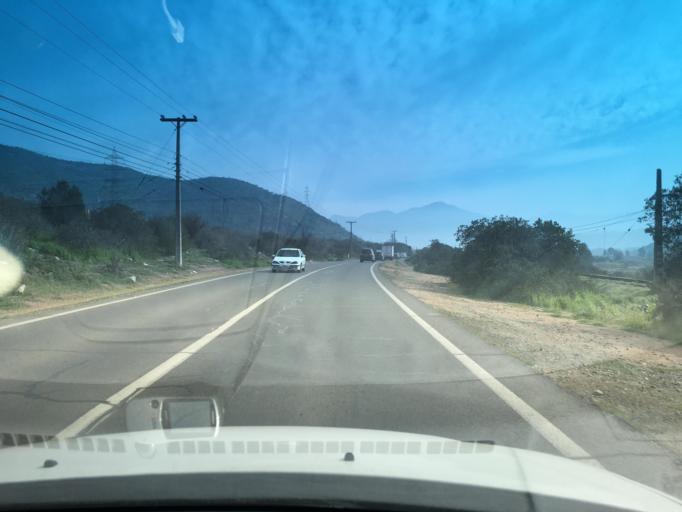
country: CL
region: Santiago Metropolitan
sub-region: Provincia de Chacabuco
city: Lampa
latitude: -33.1486
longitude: -70.9119
